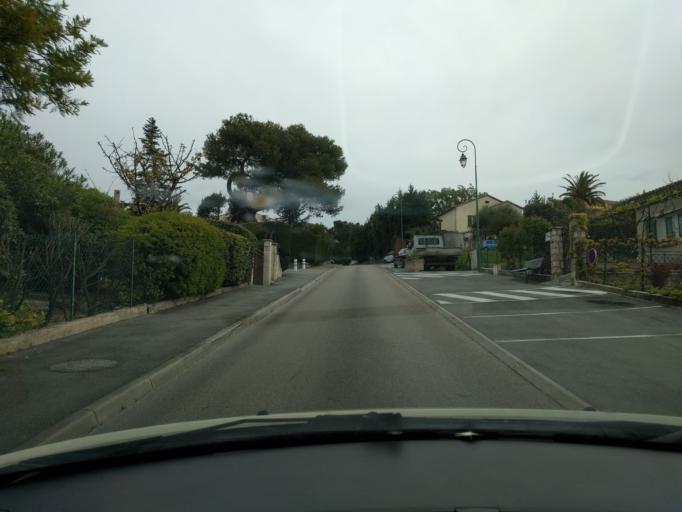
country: FR
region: Provence-Alpes-Cote d'Azur
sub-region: Departement des Alpes-Maritimes
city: La Roquette-sur-Siagne
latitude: 43.5801
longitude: 6.9513
